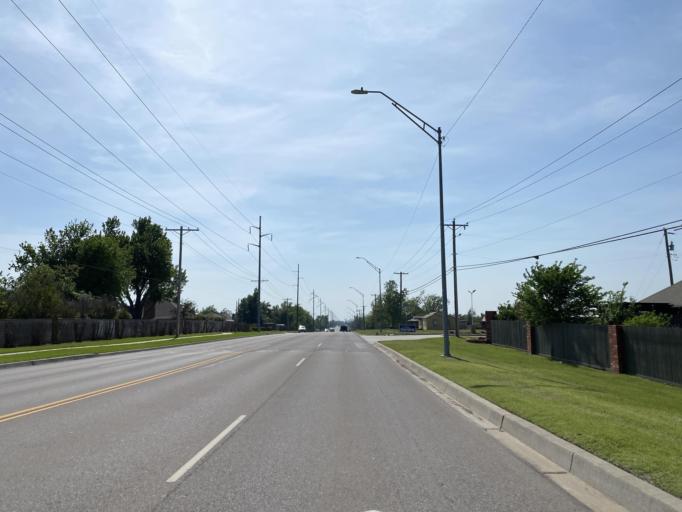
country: US
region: Oklahoma
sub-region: Oklahoma County
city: Nicoma Park
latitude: 35.4499
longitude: -97.3407
